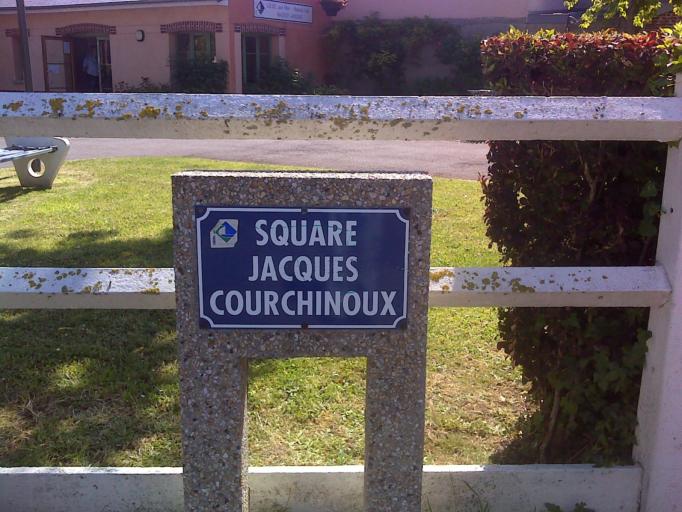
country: FR
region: Haute-Normandie
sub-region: Departement de la Seine-Maritime
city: Criel-sur-Mer
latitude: 50.0430
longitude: 1.3320
